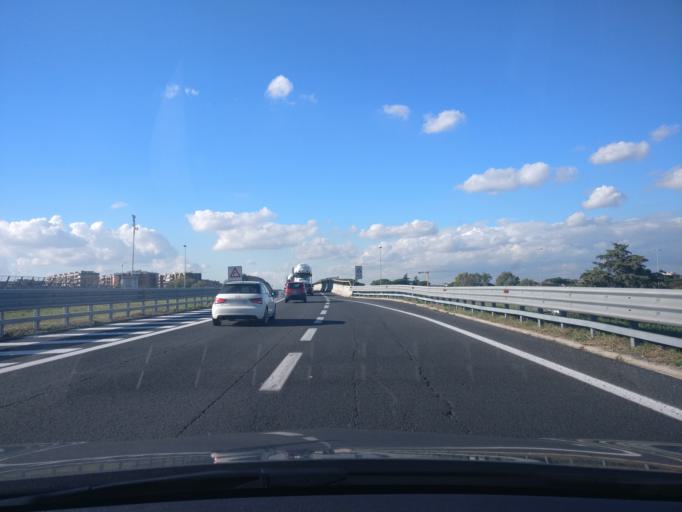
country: IT
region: Latium
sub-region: Citta metropolitana di Roma Capitale
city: Ciampino
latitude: 41.8530
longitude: 12.5984
